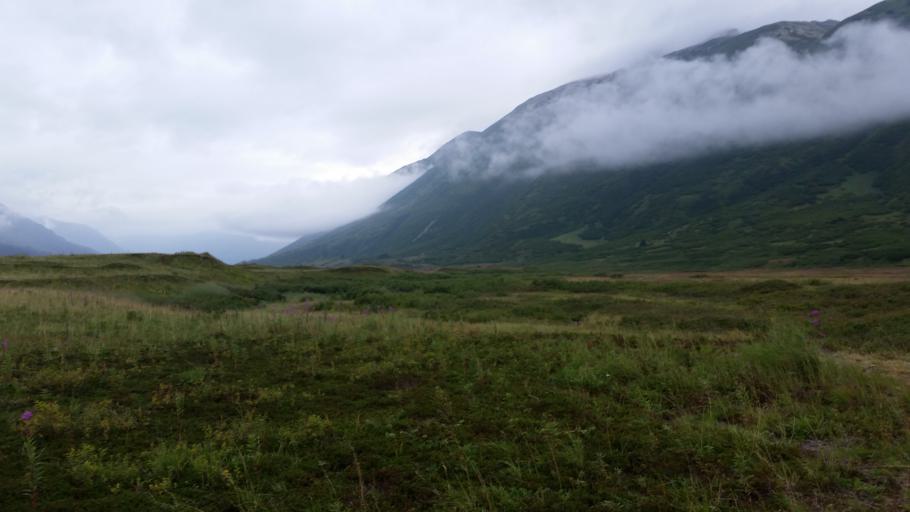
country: US
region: Alaska
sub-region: Anchorage Municipality
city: Girdwood
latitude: 60.7871
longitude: -149.2184
